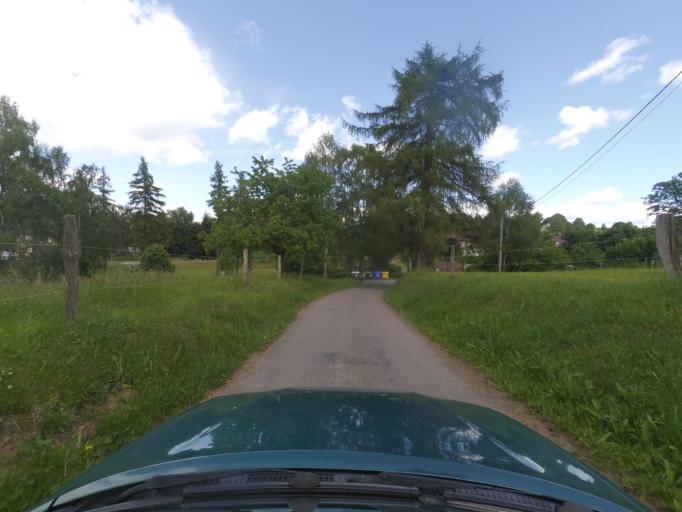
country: PL
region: Lower Silesian Voivodeship
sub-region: Powiat klodzki
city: Miedzylesie
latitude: 50.1211
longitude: 16.5994
